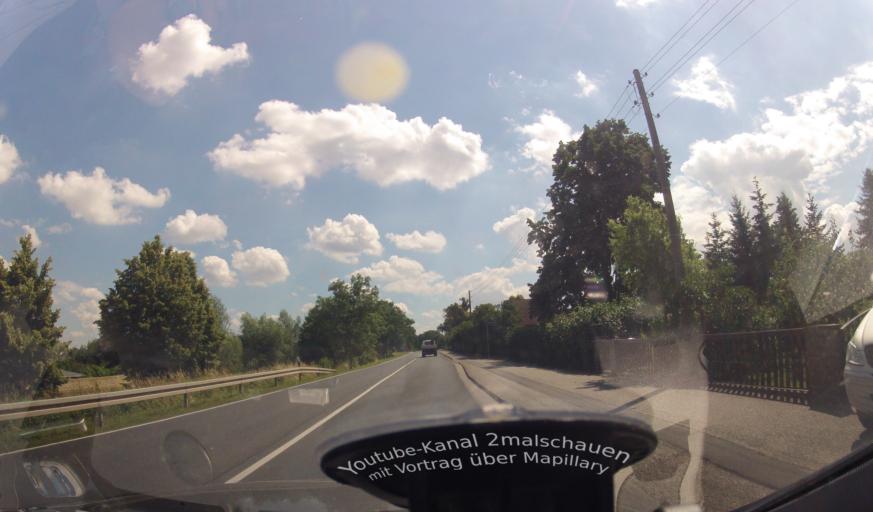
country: DE
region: Saxony
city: Torgau
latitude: 51.5465
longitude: 12.9980
